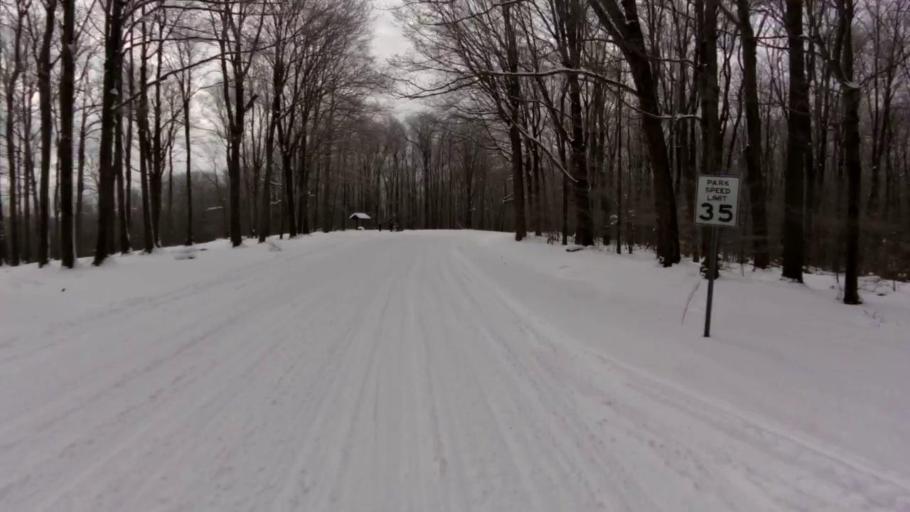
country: US
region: New York
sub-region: Cattaraugus County
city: Salamanca
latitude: 42.0462
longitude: -78.7767
